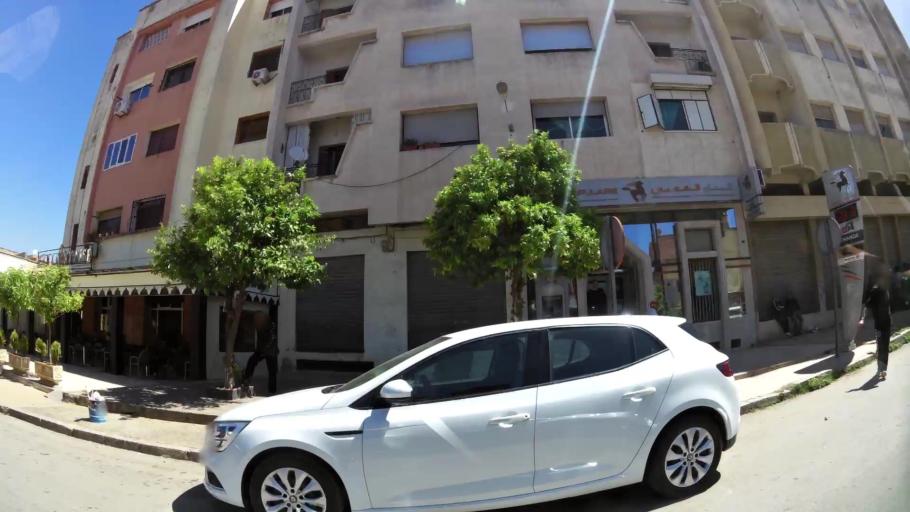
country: MA
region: Meknes-Tafilalet
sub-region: Meknes
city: Meknes
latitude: 33.9058
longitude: -5.5246
